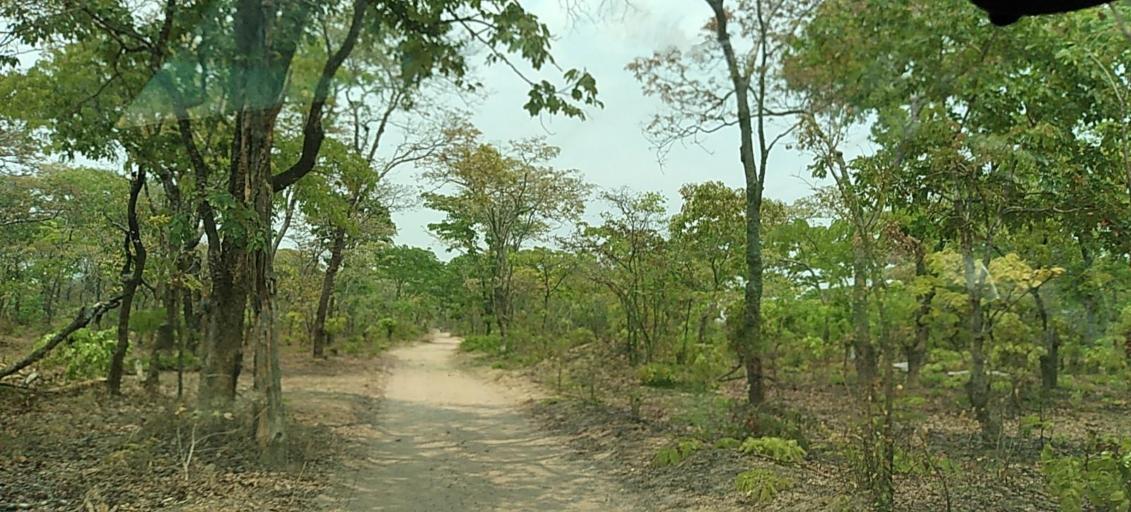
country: ZM
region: North-Western
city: Kabompo
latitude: -13.5530
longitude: 24.4485
